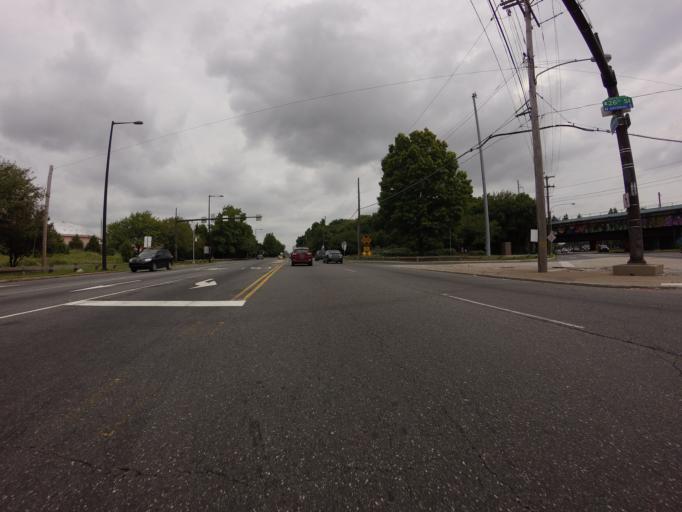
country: US
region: New Jersey
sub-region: Gloucester County
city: National Park
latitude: 39.9061
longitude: -75.1939
